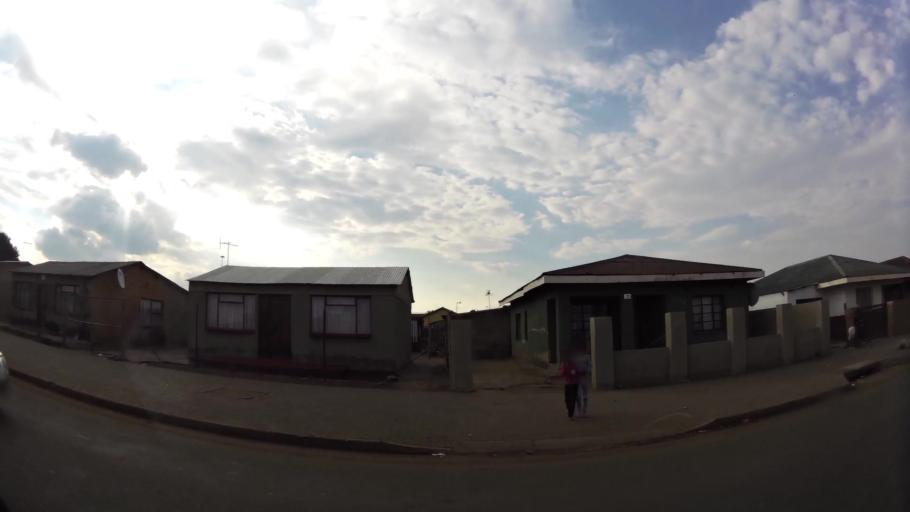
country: ZA
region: Gauteng
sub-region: Sedibeng District Municipality
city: Vanderbijlpark
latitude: -26.6974
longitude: 27.8712
